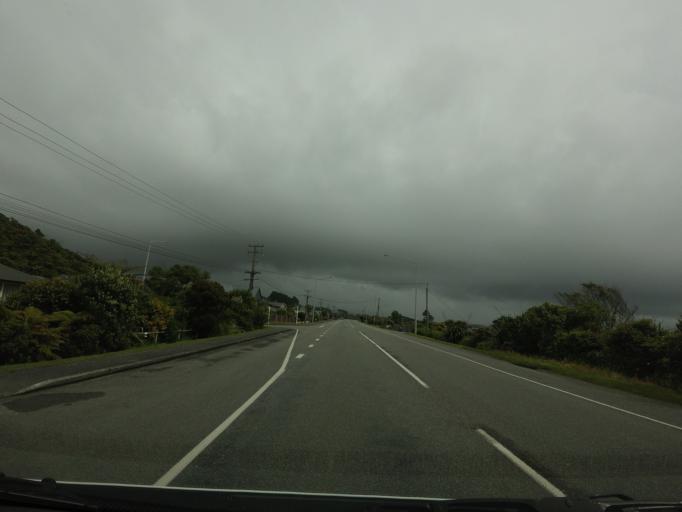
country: NZ
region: West Coast
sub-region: Grey District
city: Greymouth
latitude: -42.4835
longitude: 171.1829
